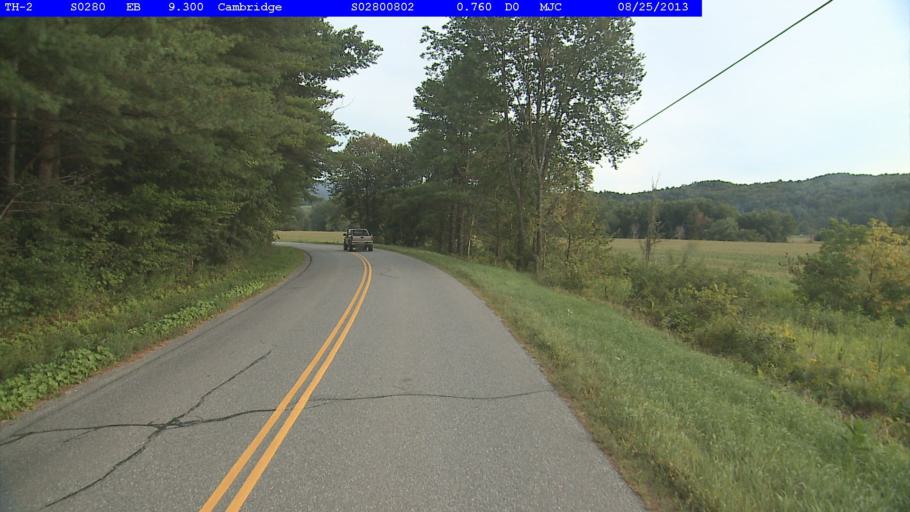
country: US
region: Vermont
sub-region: Chittenden County
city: Jericho
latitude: 44.6526
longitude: -72.8801
